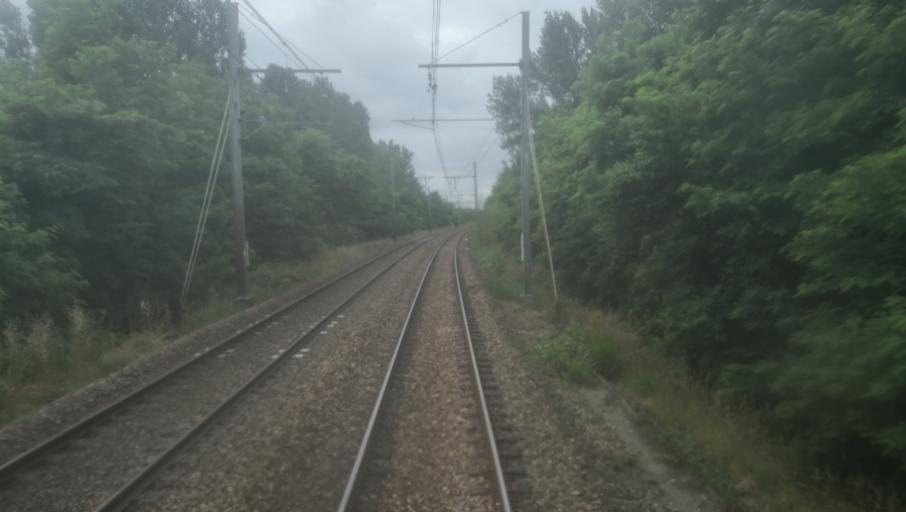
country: FR
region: Midi-Pyrenees
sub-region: Departement du Tarn-et-Garonne
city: Montbeton
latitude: 44.0149
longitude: 1.2974
